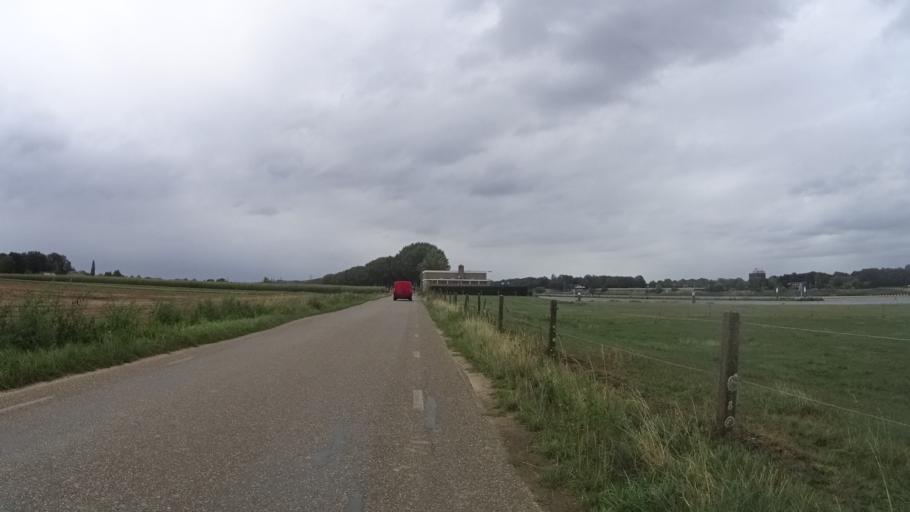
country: NL
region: Limburg
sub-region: Gemeente Beesel
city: Offenbeek
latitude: 51.3147
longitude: 6.1034
